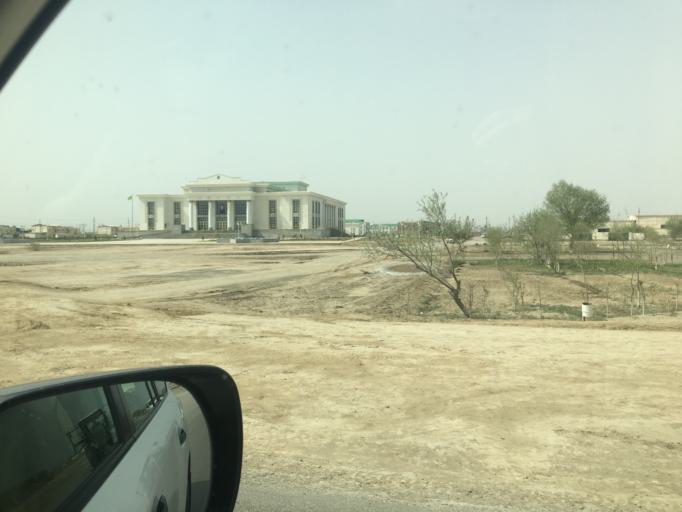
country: TM
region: Ahal
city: Tejen
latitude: 37.3680
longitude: 60.4919
